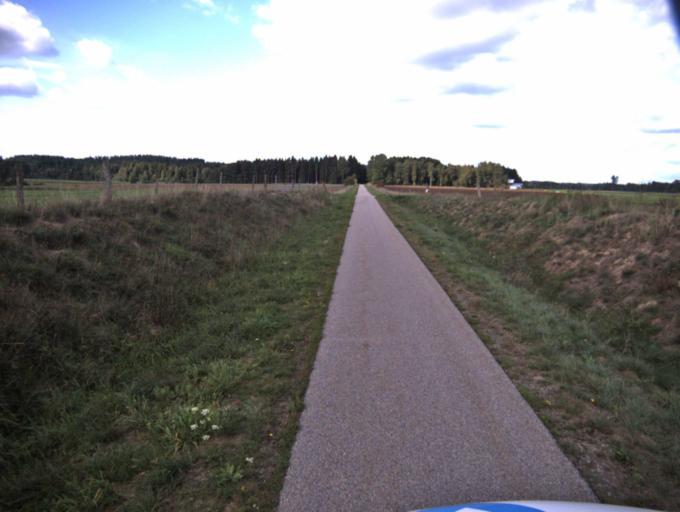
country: SE
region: Vaestra Goetaland
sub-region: Ulricehamns Kommun
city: Ulricehamn
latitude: 57.8698
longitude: 13.4285
